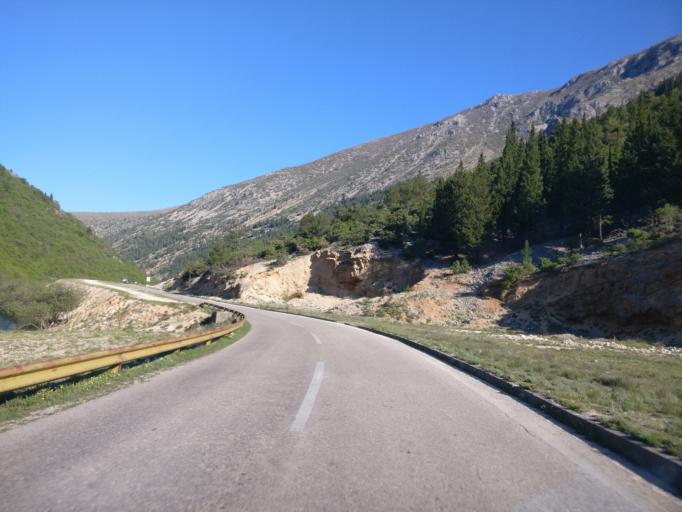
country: BA
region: Federation of Bosnia and Herzegovina
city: Stolac
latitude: 43.0938
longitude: 17.9940
